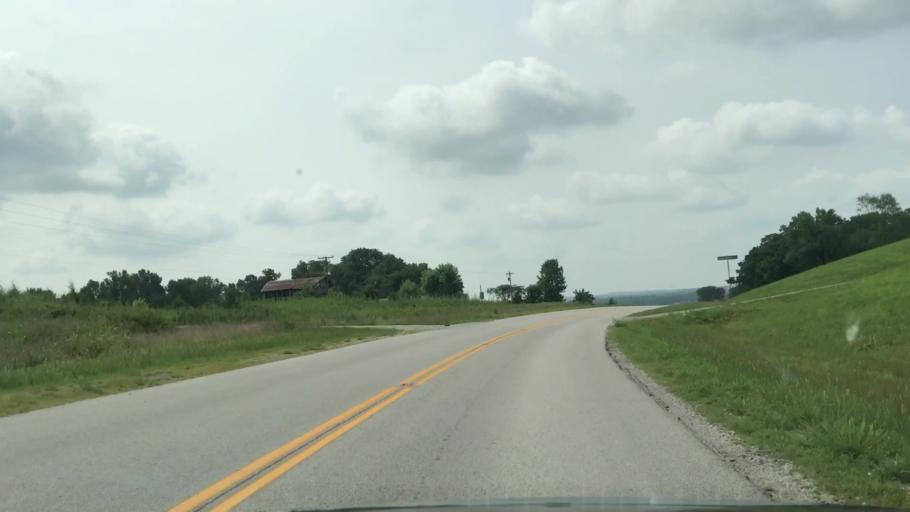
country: US
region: Kentucky
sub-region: Edmonson County
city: Brownsville
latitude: 37.1063
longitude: -86.1460
